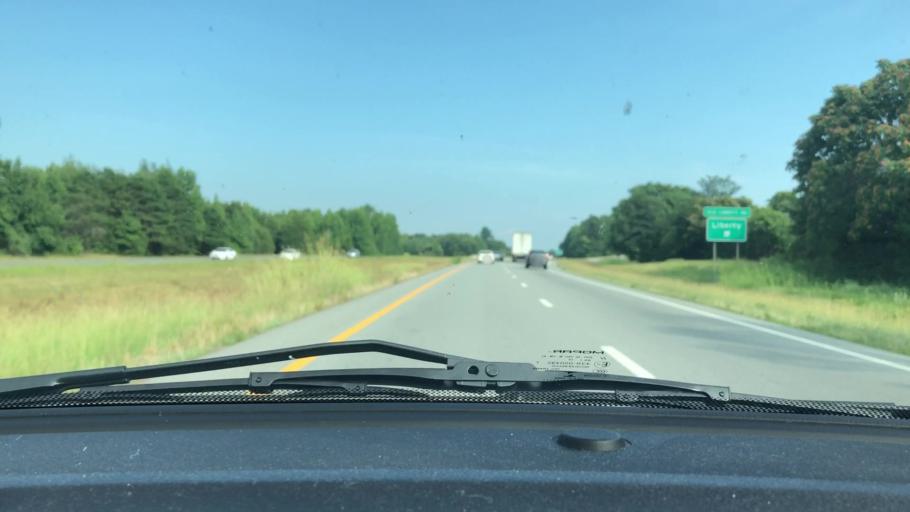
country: US
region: North Carolina
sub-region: Randolph County
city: Liberty
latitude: 35.8529
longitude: -79.6095
